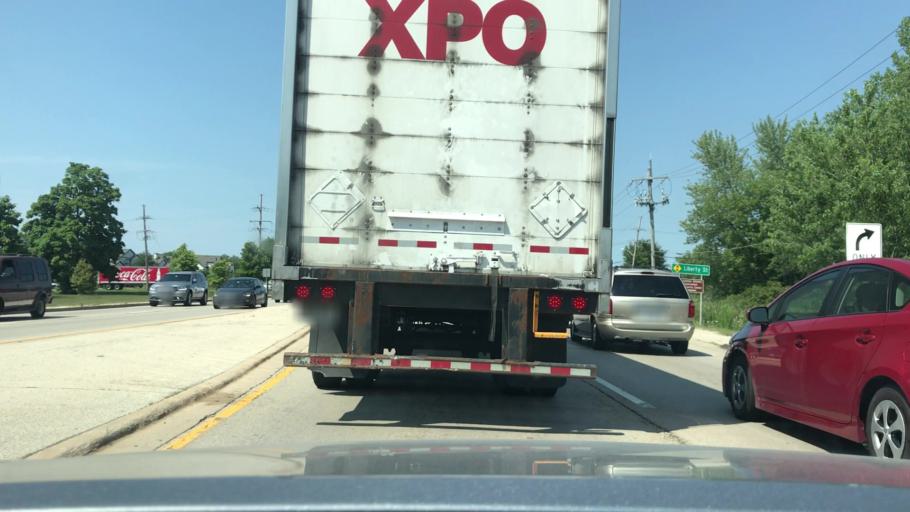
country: US
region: Illinois
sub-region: Kane County
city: Aurora
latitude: 41.7653
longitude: -88.2426
